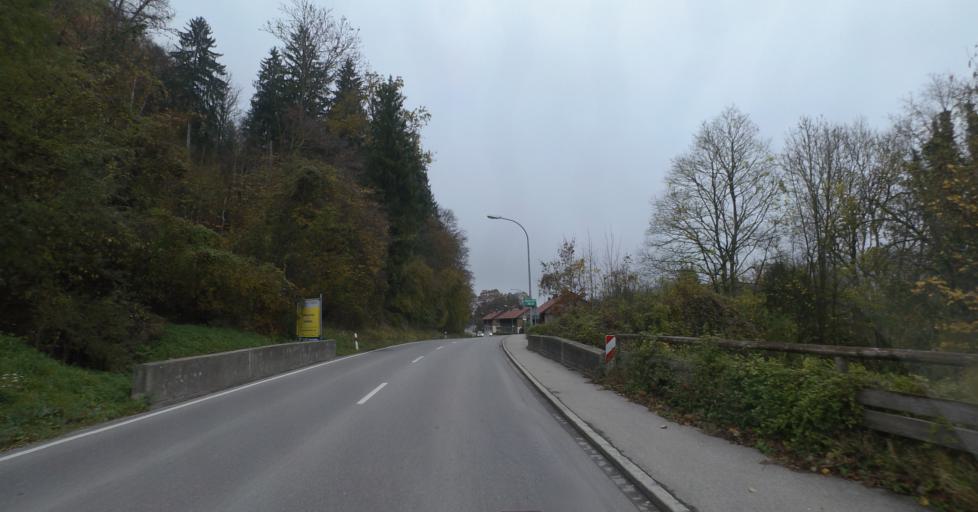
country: DE
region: Bavaria
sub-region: Upper Bavaria
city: Trostberg an der Alz
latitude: 48.0375
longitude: 12.5604
